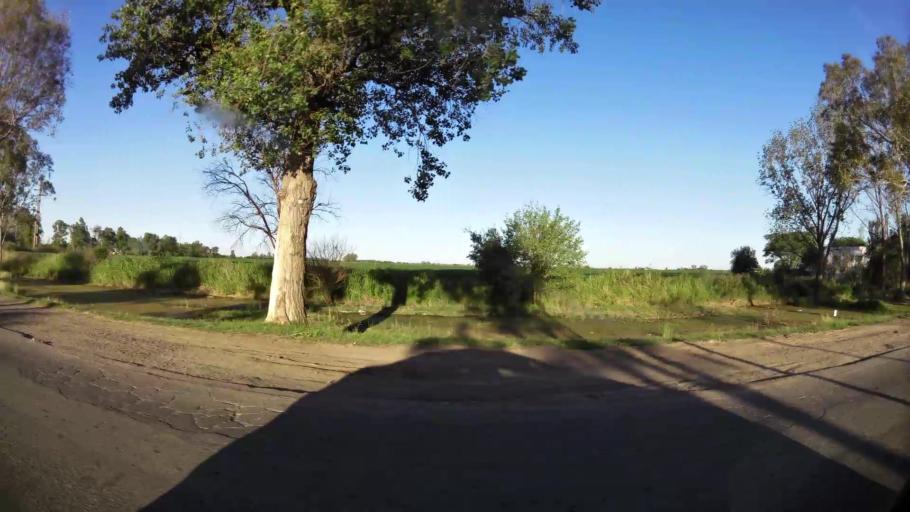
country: AR
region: Cordoba
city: Las Varillas
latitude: -31.8671
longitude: -62.7080
